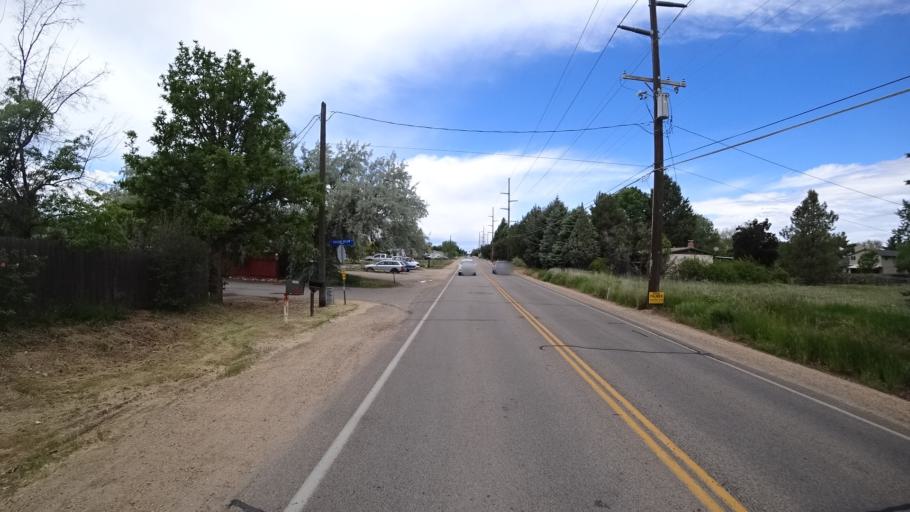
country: US
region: Idaho
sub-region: Ada County
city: Meridian
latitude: 43.5757
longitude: -116.3291
